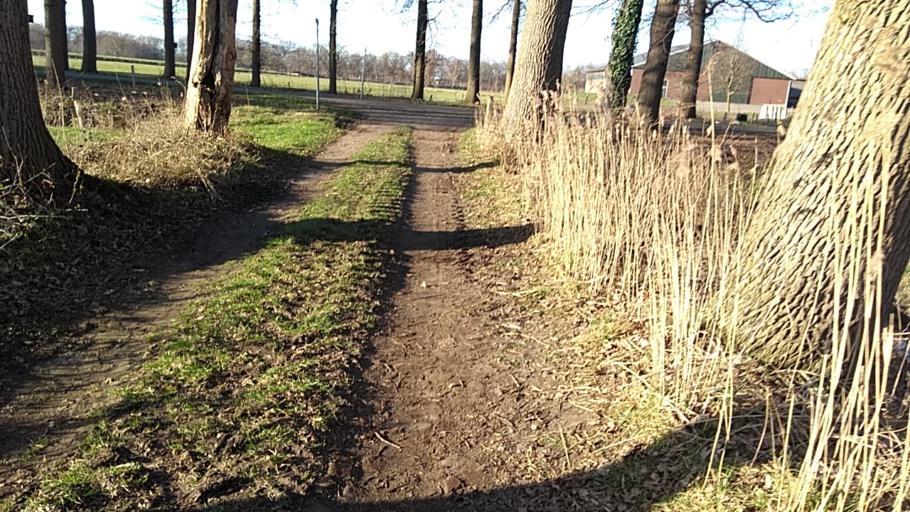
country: NL
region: Overijssel
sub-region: Gemeente Almelo
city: Almelo
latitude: 52.3643
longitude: 6.7093
